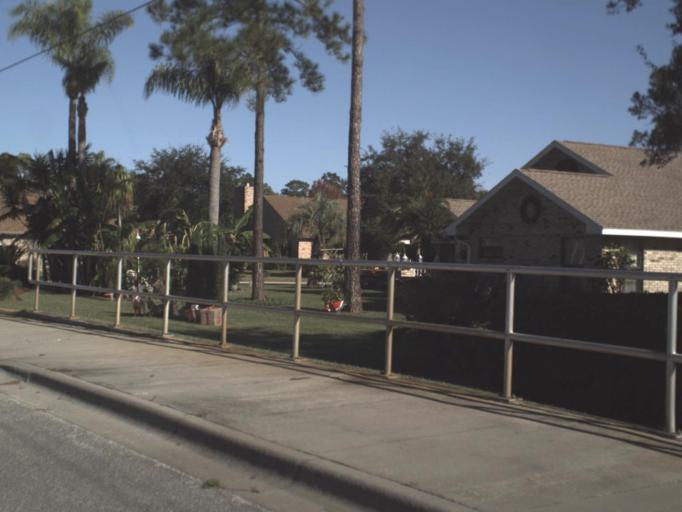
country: US
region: Florida
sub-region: Volusia County
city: Ormond Beach
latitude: 29.2678
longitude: -81.0941
